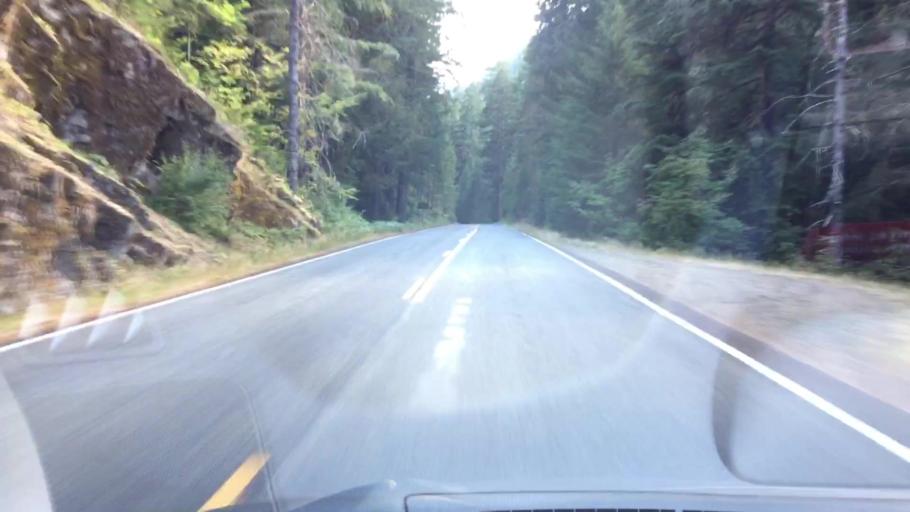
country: US
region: Washington
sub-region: Pierce County
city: Buckley
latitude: 46.7211
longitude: -121.5765
